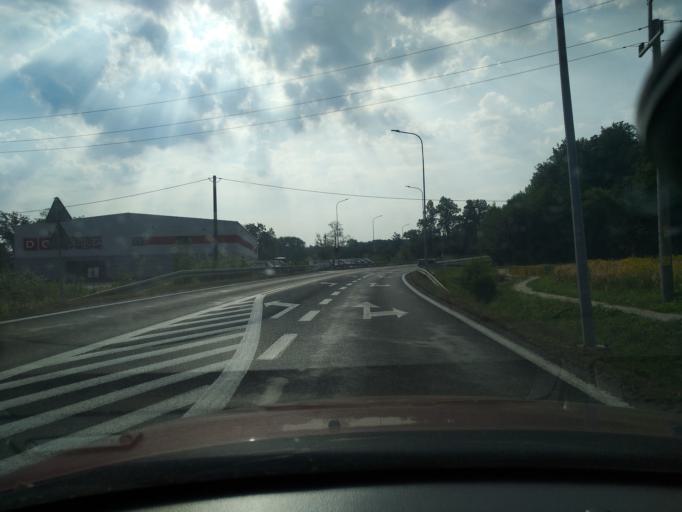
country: PL
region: Lower Silesian Voivodeship
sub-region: Powiat lubanski
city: Olszyna
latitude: 51.0650
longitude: 15.3712
